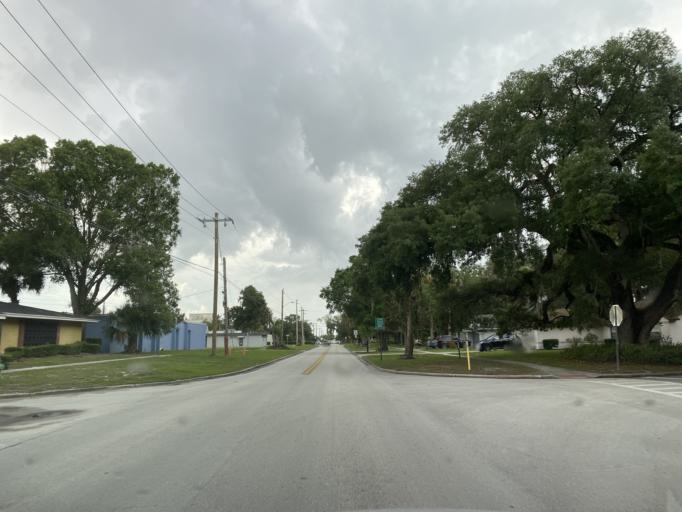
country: US
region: Florida
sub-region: Seminole County
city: Sanford
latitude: 28.8083
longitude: -81.2551
